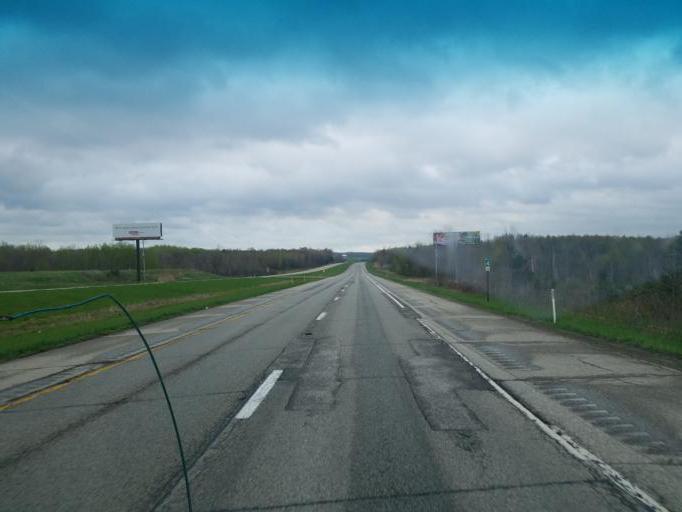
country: US
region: Pennsylvania
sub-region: Erie County
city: North East
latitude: 42.1339
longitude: -79.8152
